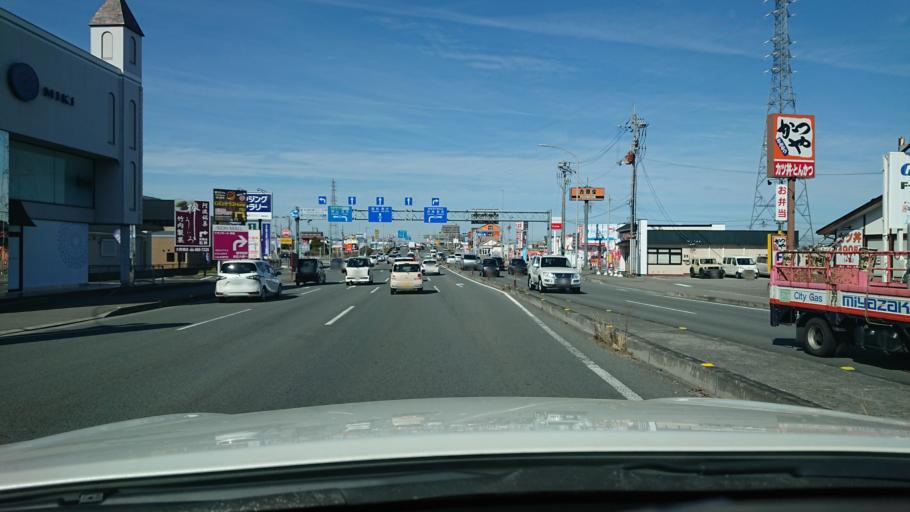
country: JP
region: Tokushima
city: Tokushima-shi
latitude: 34.0415
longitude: 134.5520
